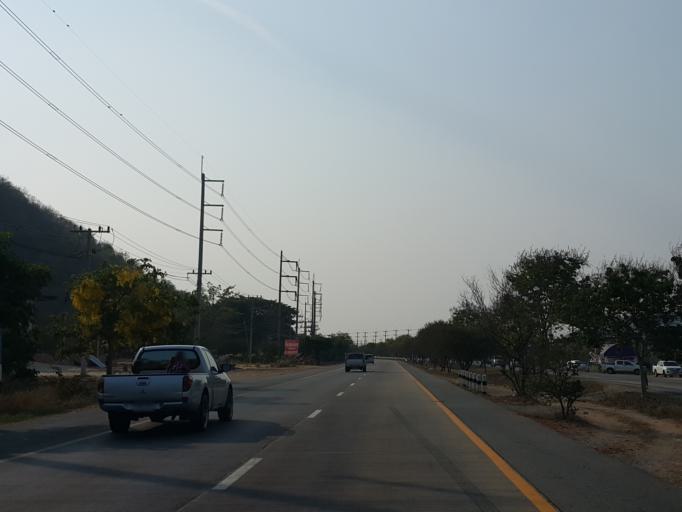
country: TH
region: Suphan Buri
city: Doembang Nangbuat
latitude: 14.8387
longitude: 100.1083
